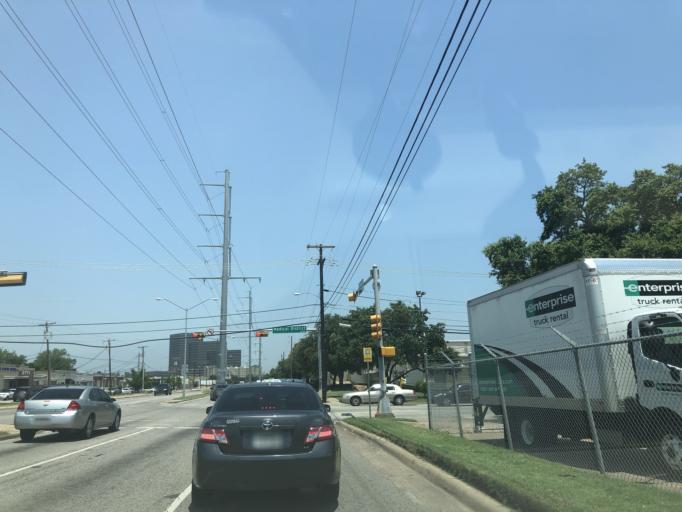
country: US
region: Texas
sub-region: Dallas County
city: Dallas
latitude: 32.8028
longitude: -96.8434
